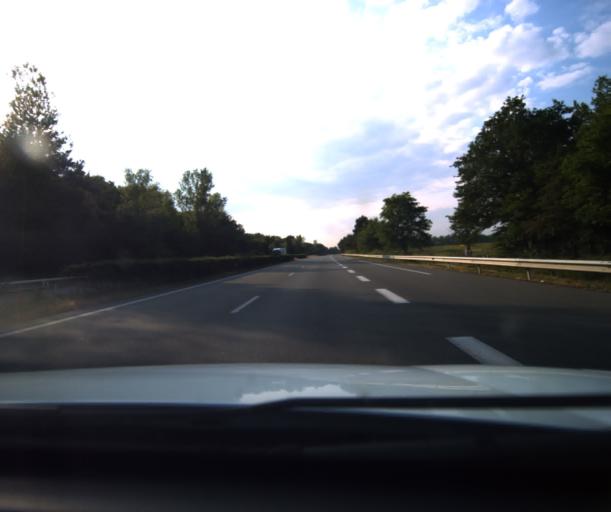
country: FR
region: Midi-Pyrenees
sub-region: Departement du Tarn-et-Garonne
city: Montech
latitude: 43.9649
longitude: 1.2740
